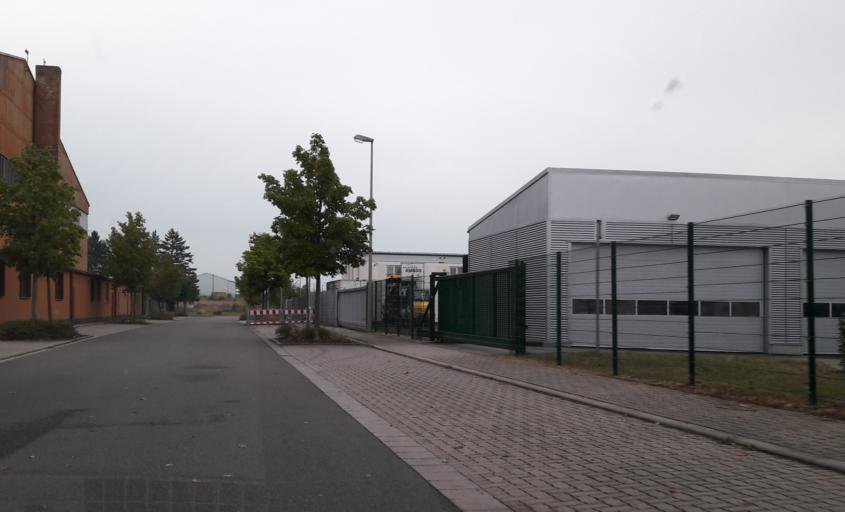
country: DE
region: Rheinland-Pfalz
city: Zweibrucken
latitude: 49.2228
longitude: 7.3996
